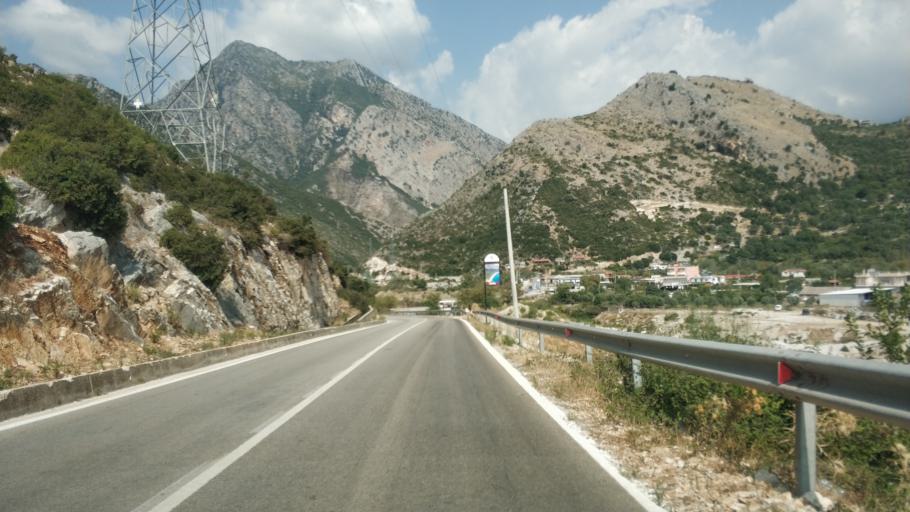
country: AL
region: Vlore
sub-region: Rrethi i Sarandes
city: Lukove
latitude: 40.0603
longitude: 19.8485
